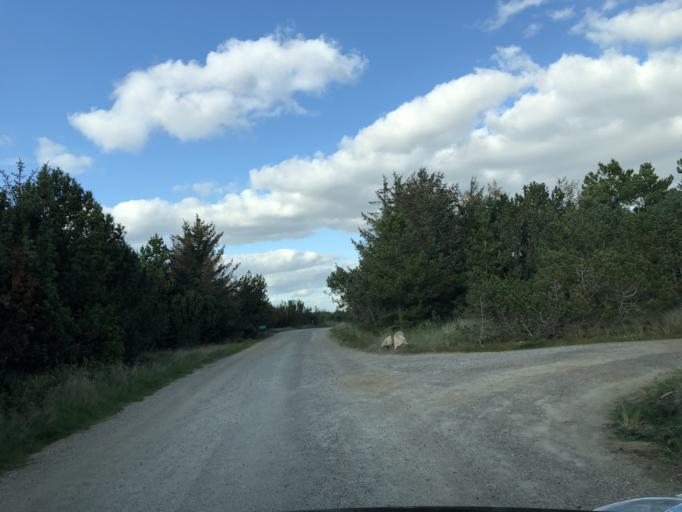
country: DK
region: Central Jutland
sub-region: Holstebro Kommune
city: Ulfborg
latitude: 56.3226
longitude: 8.1384
